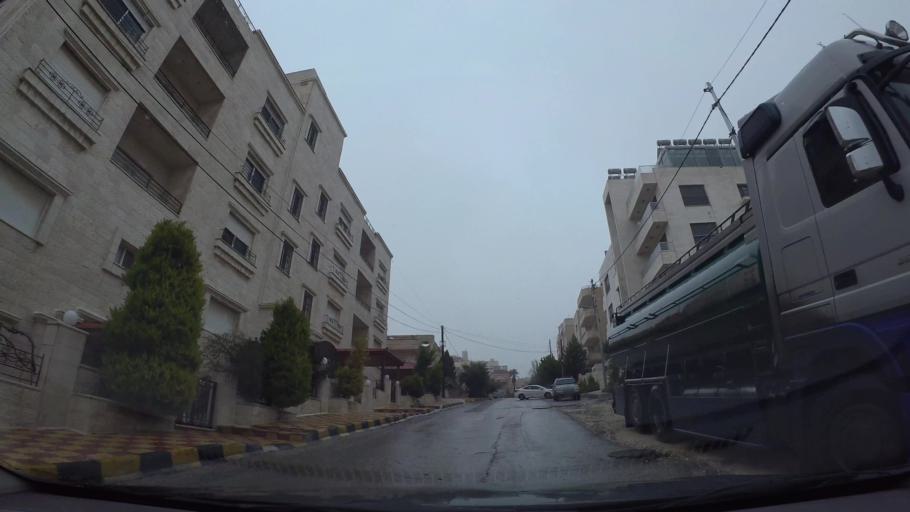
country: JO
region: Amman
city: Al Jubayhah
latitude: 32.0287
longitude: 35.8814
